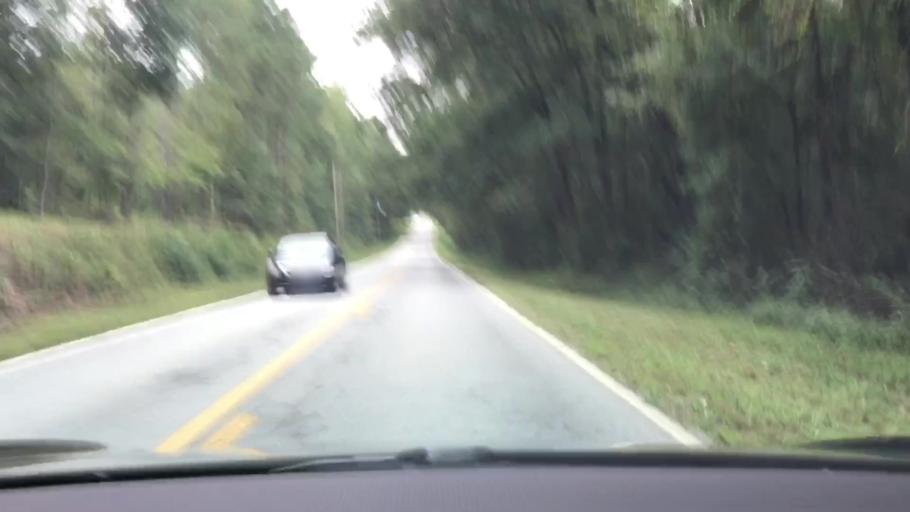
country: US
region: Georgia
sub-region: Barrow County
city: Auburn
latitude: 34.0542
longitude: -83.8228
